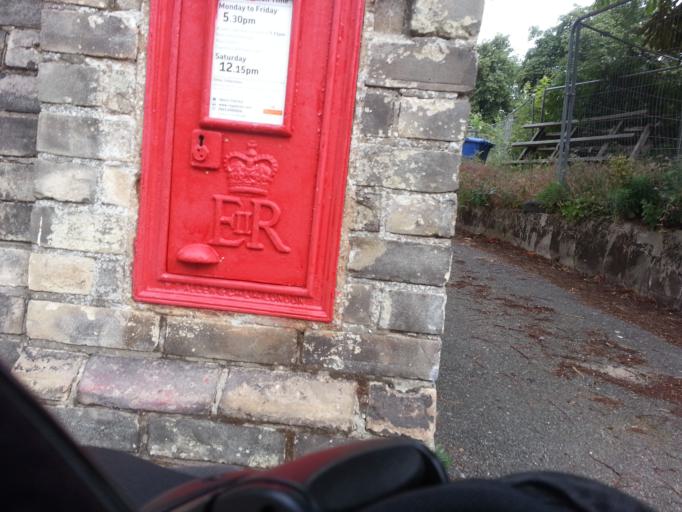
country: GB
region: England
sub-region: Suffolk
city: Ipswich
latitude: 52.0585
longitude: 1.1430
